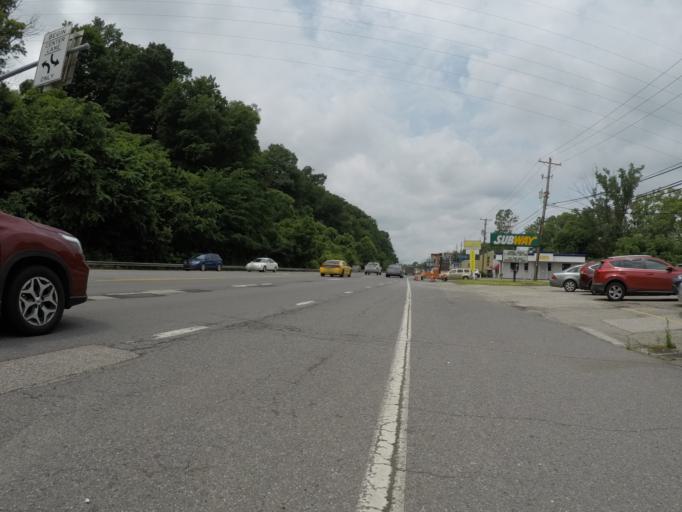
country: US
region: West Virginia
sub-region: Cabell County
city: Pea Ridge
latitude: 38.4132
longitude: -82.3544
